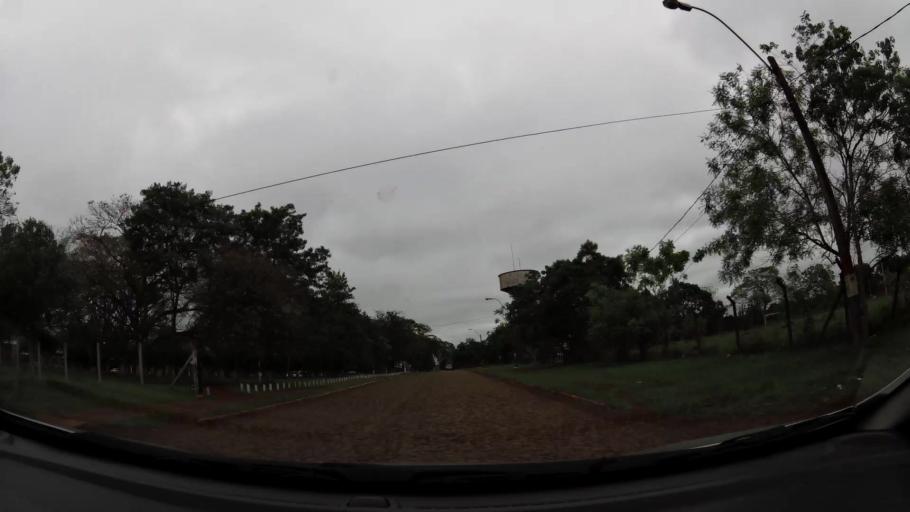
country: PY
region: Alto Parana
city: Presidente Franco
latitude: -25.4864
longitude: -54.7949
